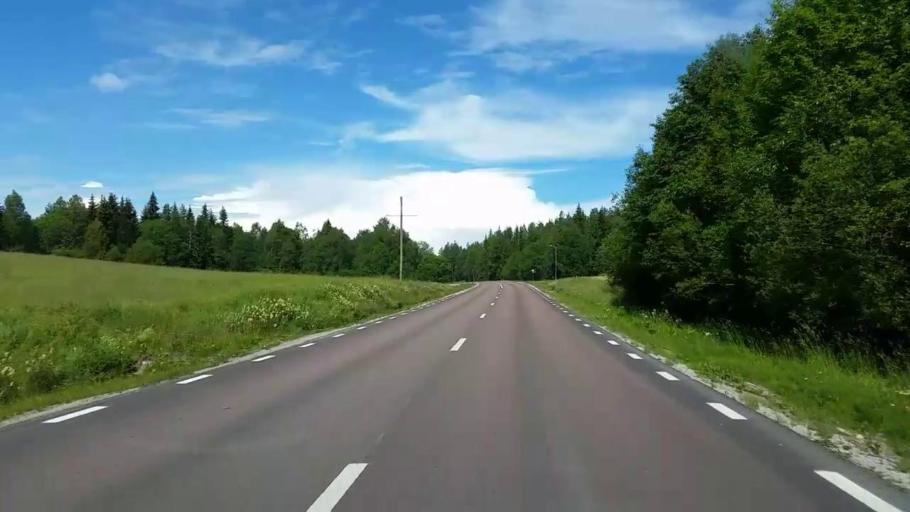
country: SE
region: Dalarna
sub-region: Rattviks Kommun
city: Raettvik
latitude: 61.0237
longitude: 15.2096
